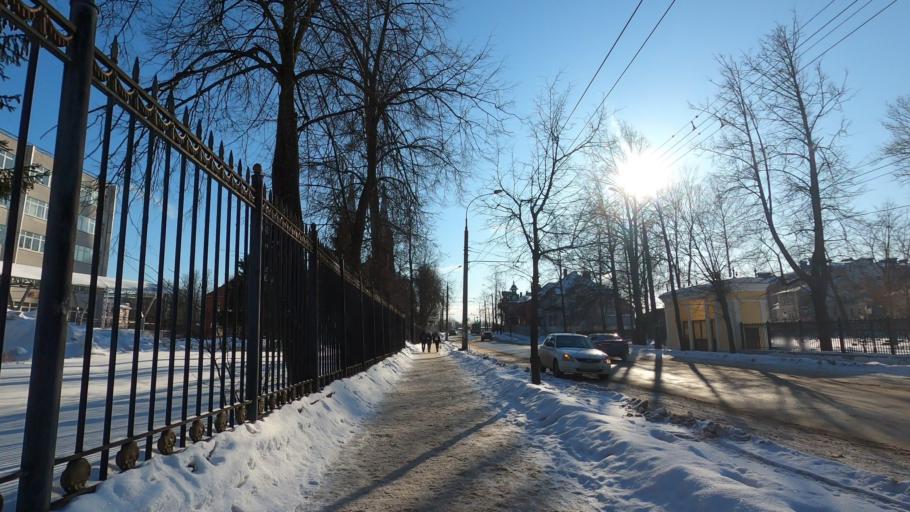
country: RU
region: Jaroslavl
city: Rybinsk
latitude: 58.0449
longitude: 38.8378
